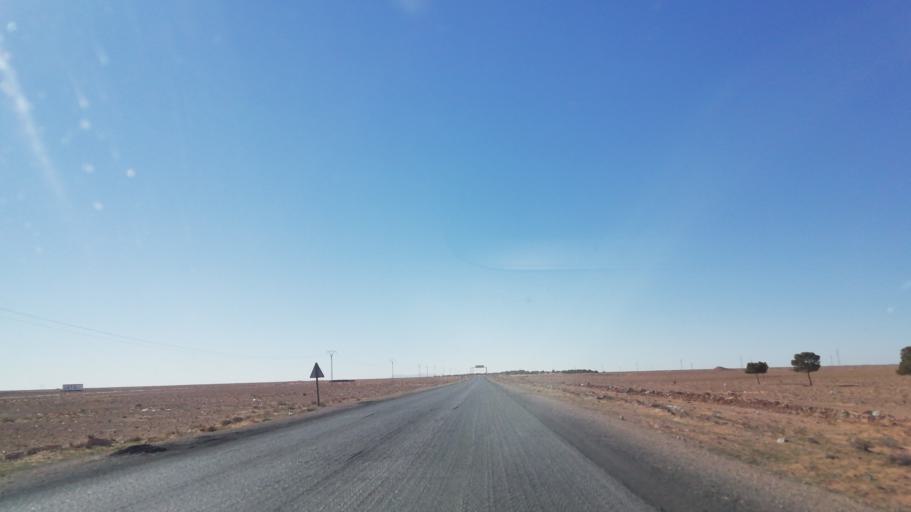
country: DZ
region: Saida
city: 'Ain el Hadjar
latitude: 34.0106
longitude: 0.0534
